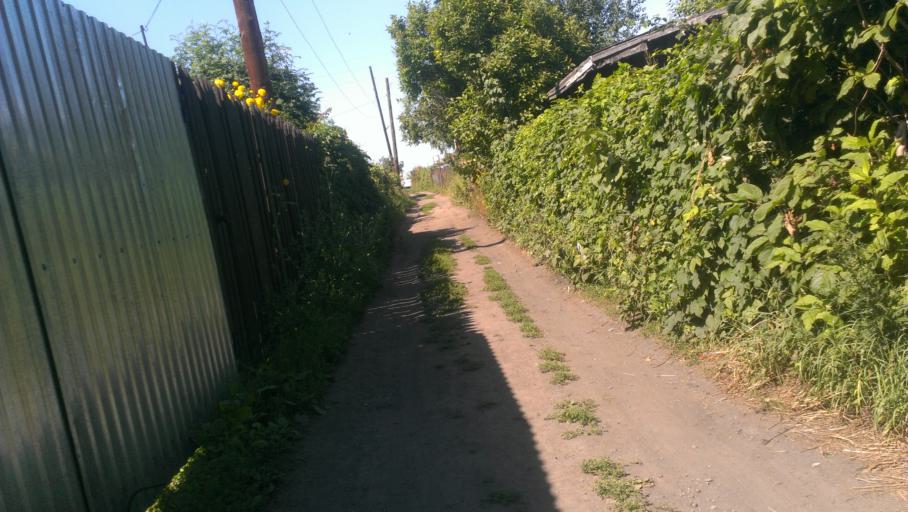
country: RU
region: Altai Krai
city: Nauchnyy Gorodok
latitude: 53.4245
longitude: 83.5065
